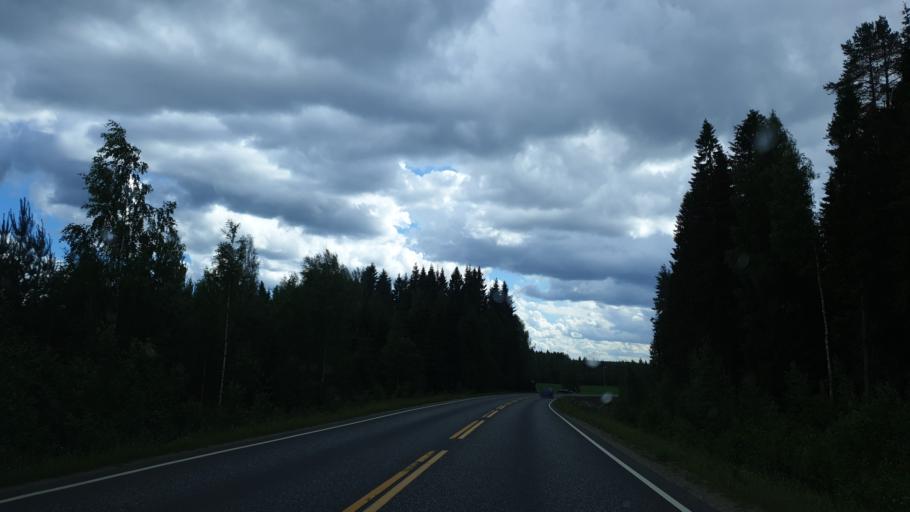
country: FI
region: Northern Savo
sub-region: Koillis-Savo
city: Kaavi
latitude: 62.9534
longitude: 28.4014
